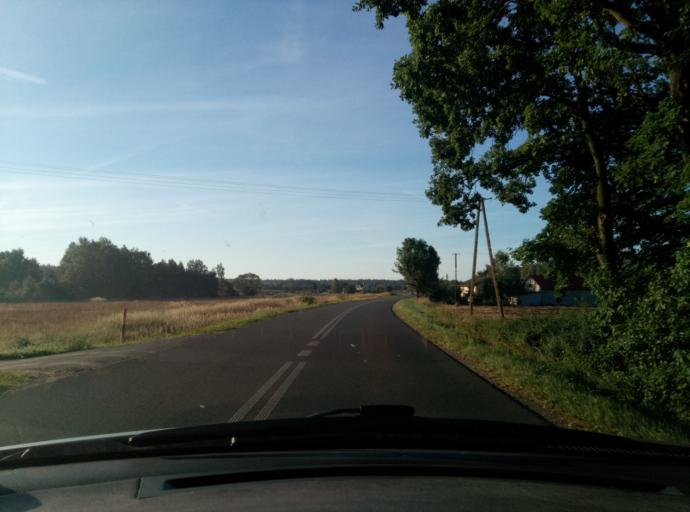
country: PL
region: Kujawsko-Pomorskie
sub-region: Powiat wabrzeski
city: Wabrzezno
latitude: 53.2453
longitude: 18.9381
